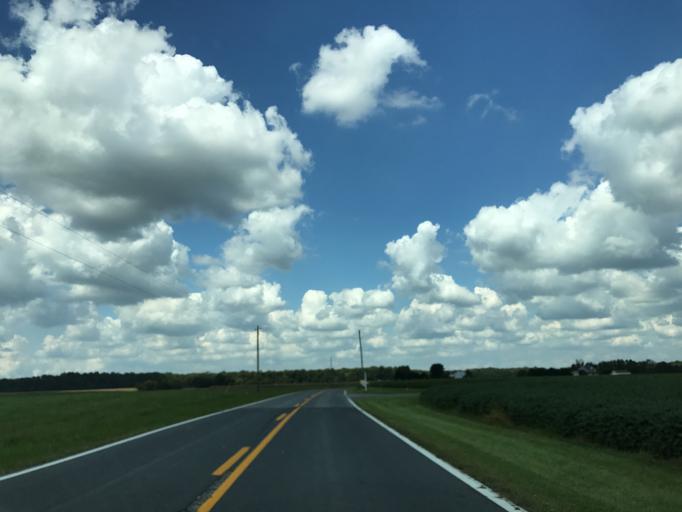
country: US
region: Maryland
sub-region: Caroline County
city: Ridgely
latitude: 39.0445
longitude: -75.9159
